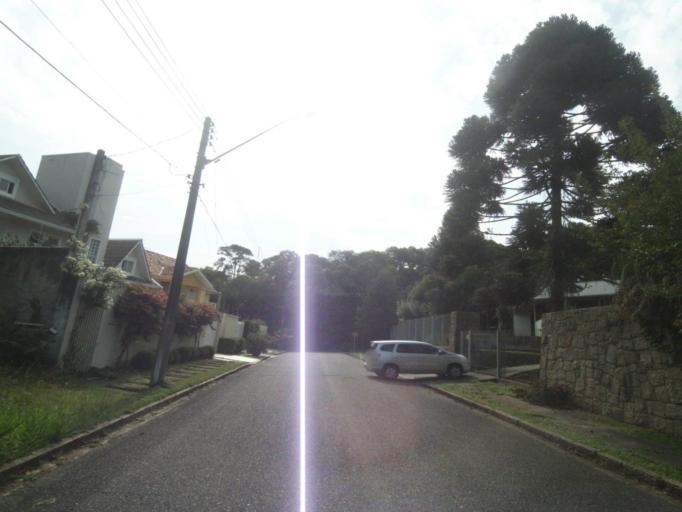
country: BR
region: Parana
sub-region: Curitiba
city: Curitiba
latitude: -25.4107
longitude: -49.3145
